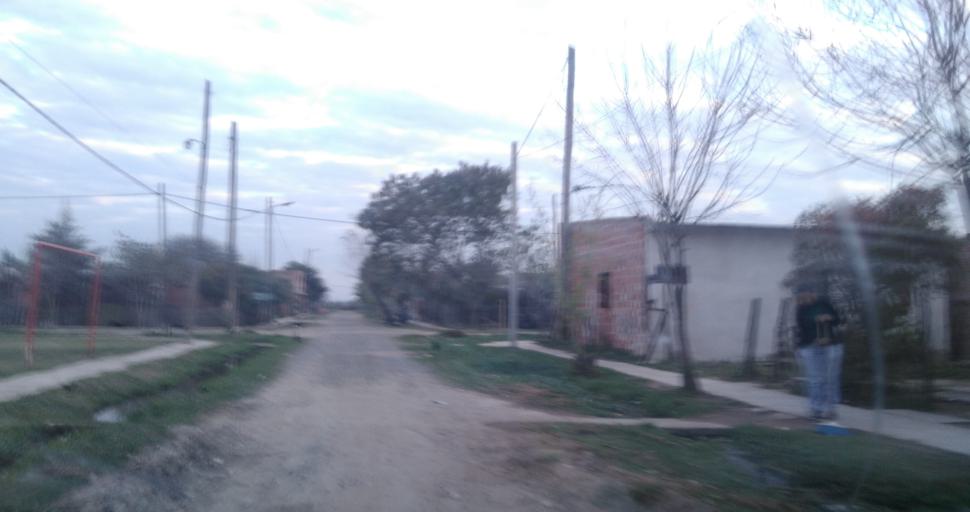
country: AR
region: Chaco
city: Fontana
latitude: -27.4480
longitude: -59.0391
